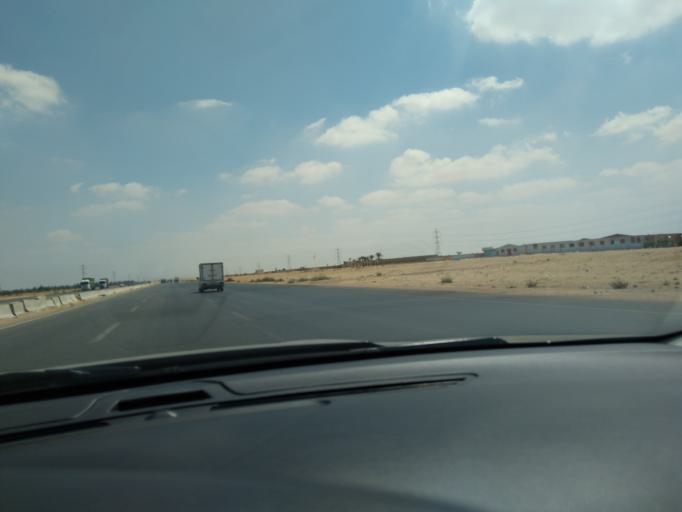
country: EG
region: Al Isma'iliyah
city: At Tall al Kabir
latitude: 30.3508
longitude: 31.8850
